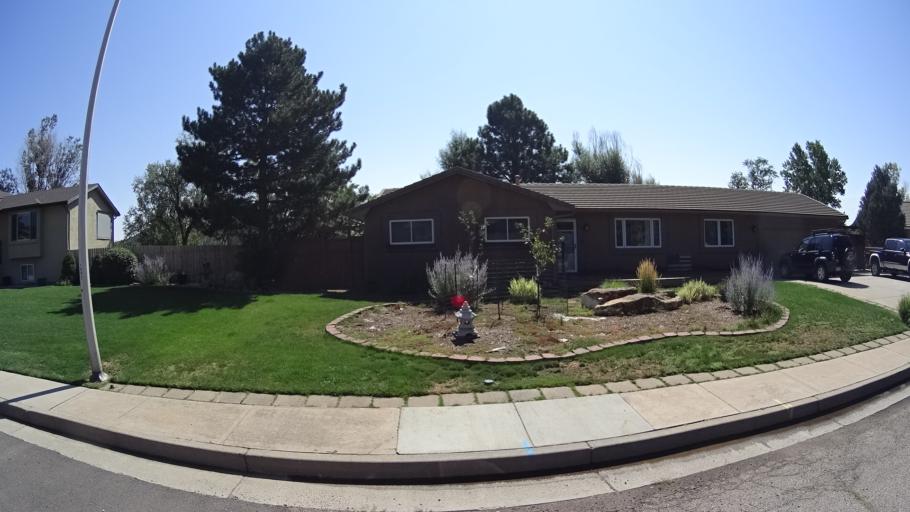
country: US
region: Colorado
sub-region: El Paso County
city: Air Force Academy
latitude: 38.9200
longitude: -104.8213
